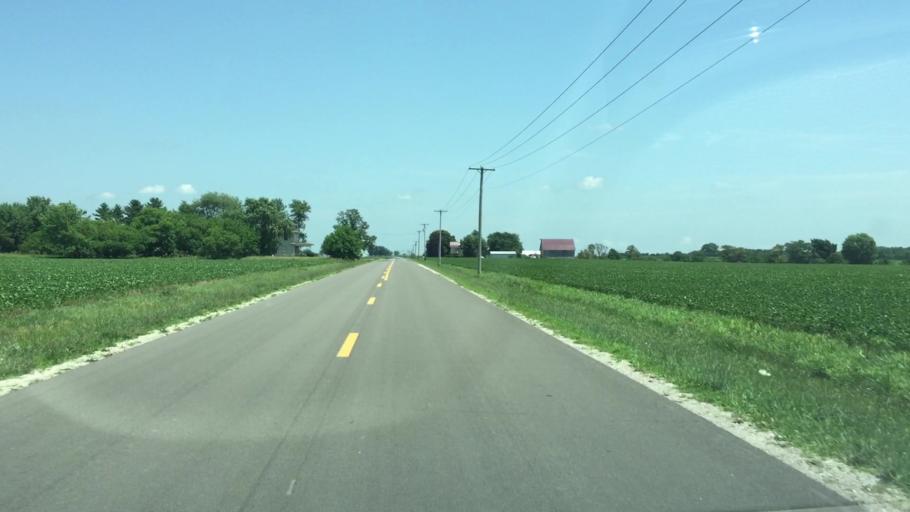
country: US
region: Illinois
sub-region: Hancock County
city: Carthage
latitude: 40.3279
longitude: -91.1744
